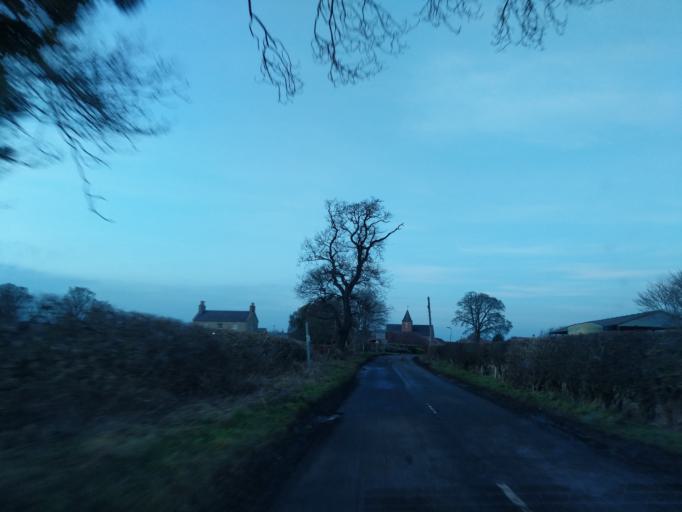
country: GB
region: Scotland
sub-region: Midlothian
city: Gorebridge
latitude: 55.8320
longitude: -3.0876
